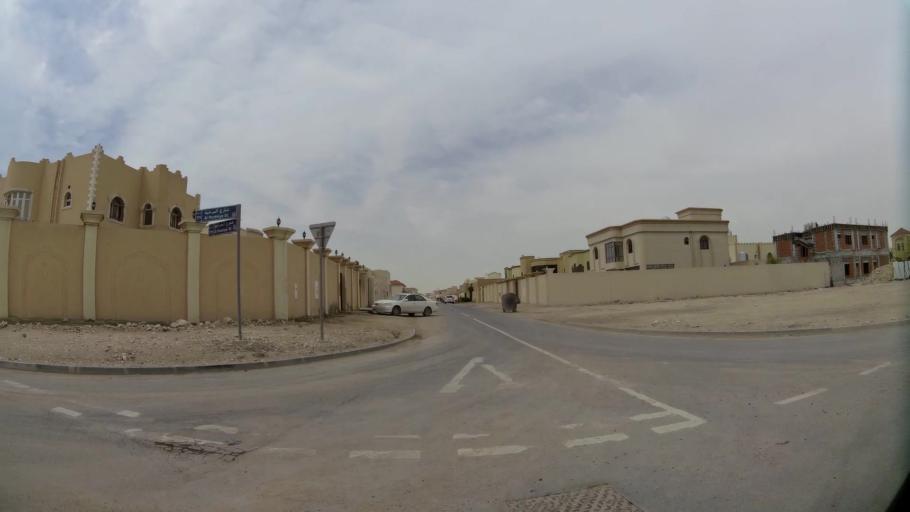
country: QA
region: Baladiyat ar Rayyan
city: Ar Rayyan
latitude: 25.2106
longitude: 51.4567
